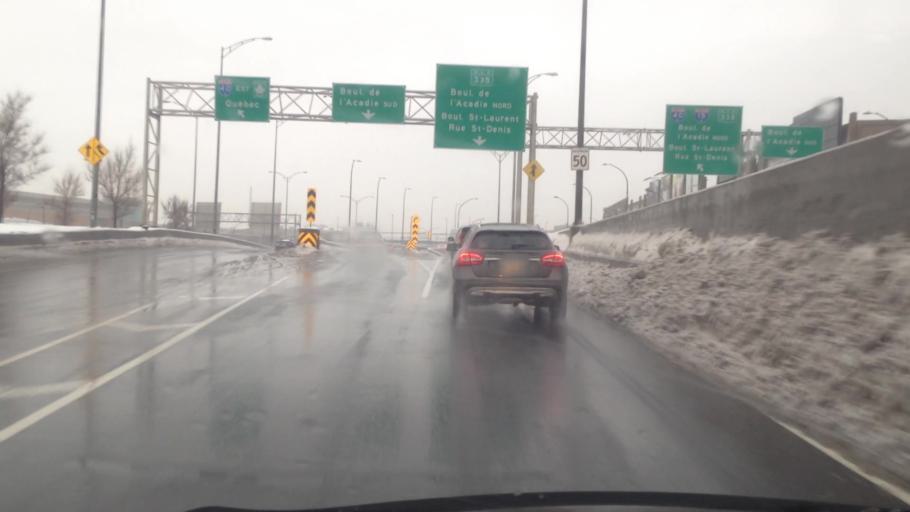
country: CA
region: Quebec
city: Mont-Royal
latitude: 45.5278
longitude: -73.6502
